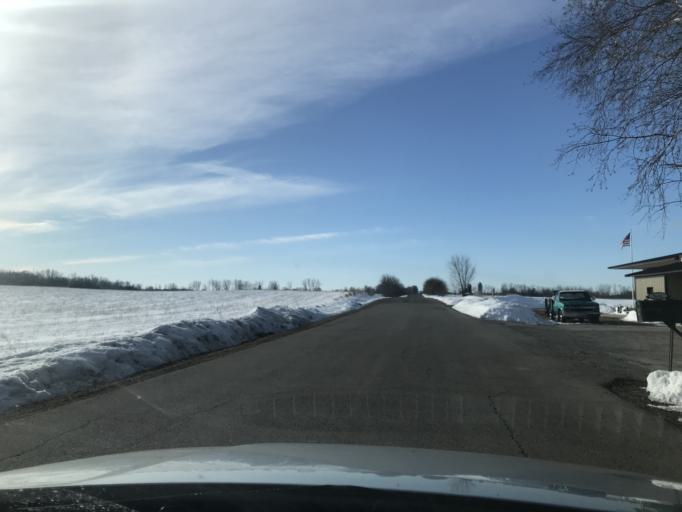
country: US
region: Wisconsin
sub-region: Oconto County
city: Oconto Falls
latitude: 44.9504
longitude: -88.0163
